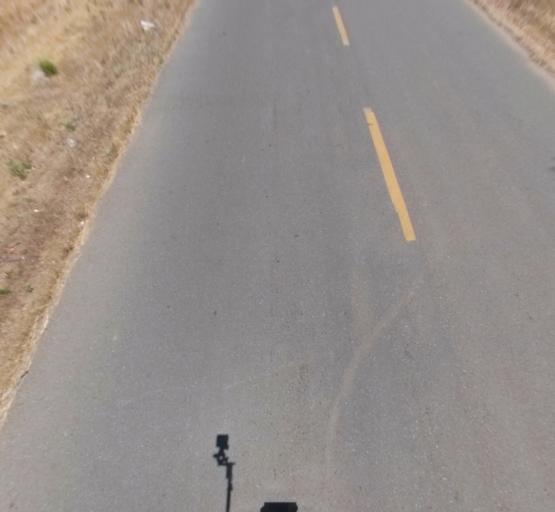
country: US
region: California
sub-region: Madera County
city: Madera
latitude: 36.9821
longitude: -120.0827
